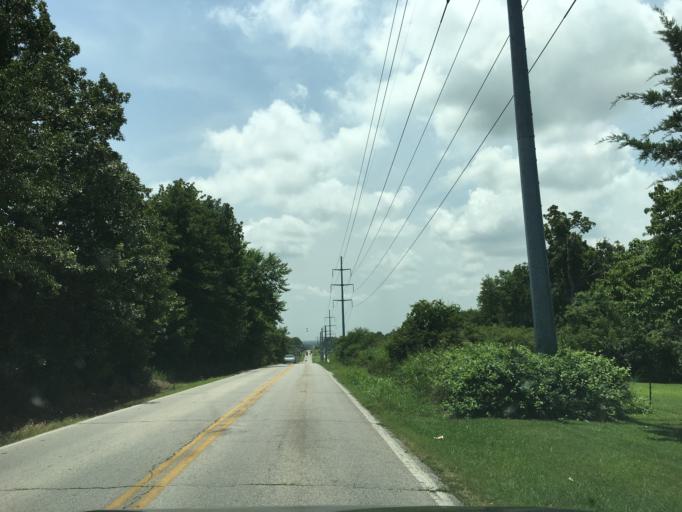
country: US
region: Oklahoma
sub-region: Tulsa County
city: Jenks
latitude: 36.0633
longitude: -95.9937
